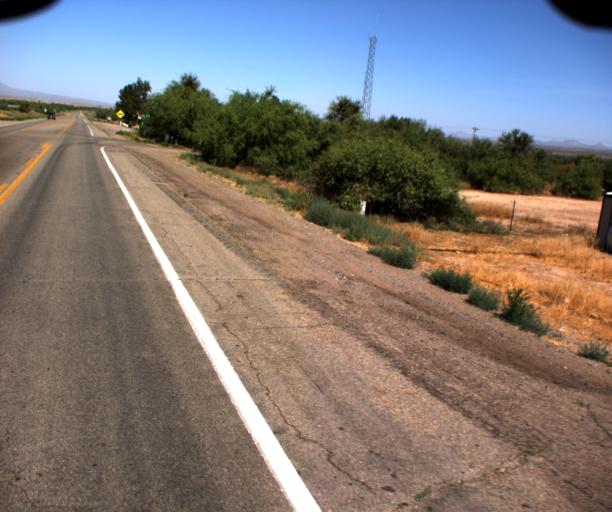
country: US
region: Arizona
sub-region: Graham County
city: Bylas
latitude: 33.0370
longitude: -109.9651
